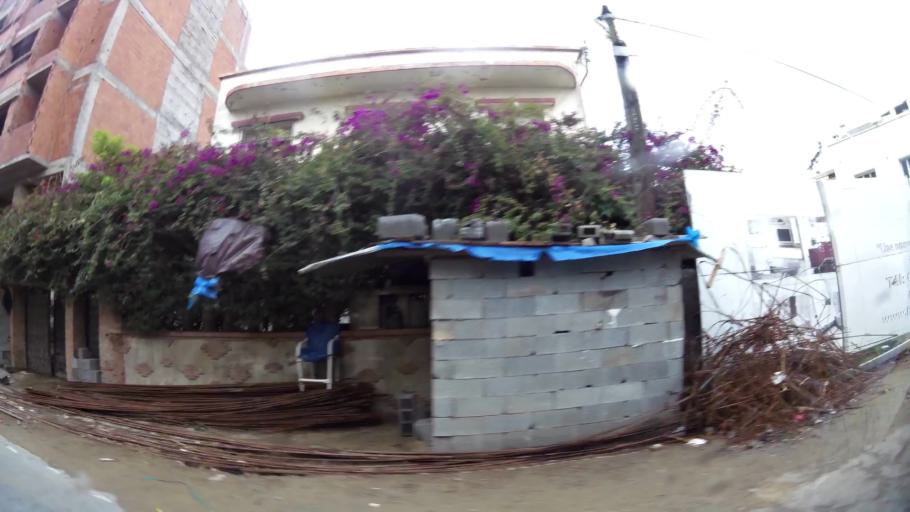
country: MA
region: Grand Casablanca
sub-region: Casablanca
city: Casablanca
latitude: 33.5709
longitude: -7.6192
